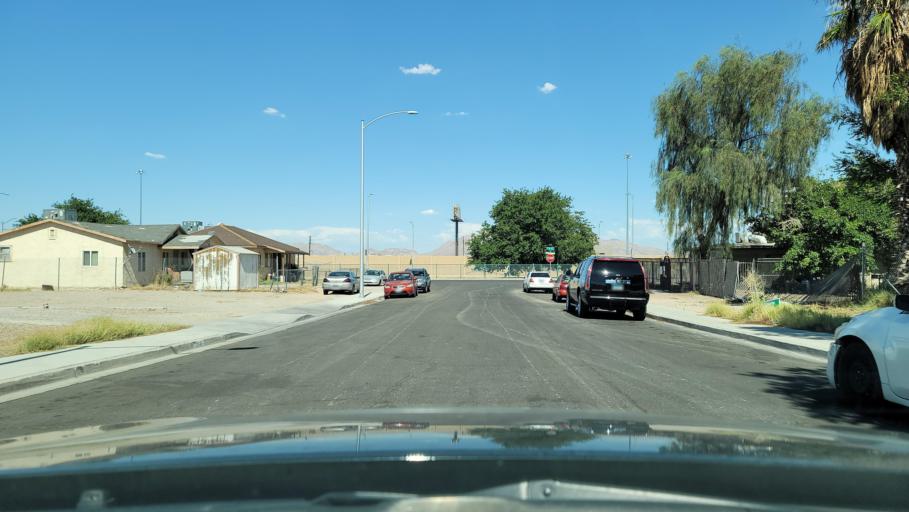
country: US
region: Nevada
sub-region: Clark County
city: Las Vegas
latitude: 36.1860
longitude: -115.1455
